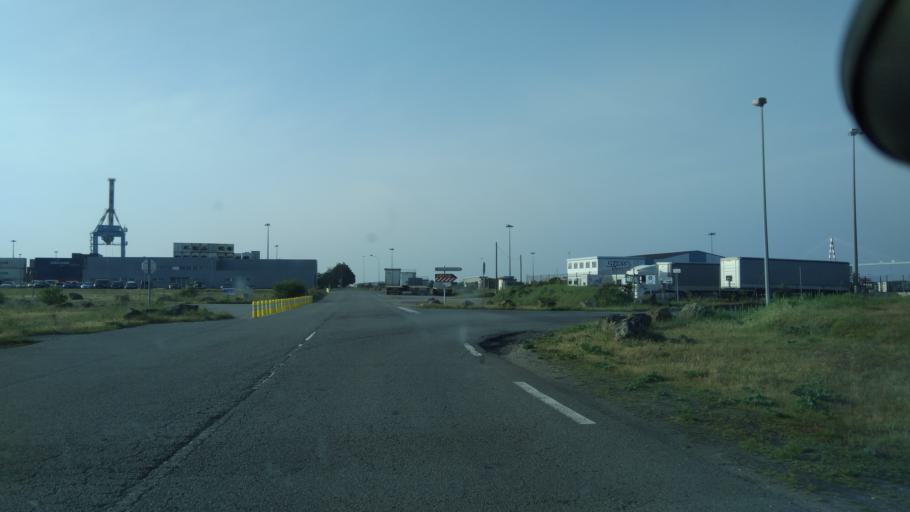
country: FR
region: Pays de la Loire
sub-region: Departement de la Loire-Atlantique
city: Trignac
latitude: 47.2987
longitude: -2.1631
